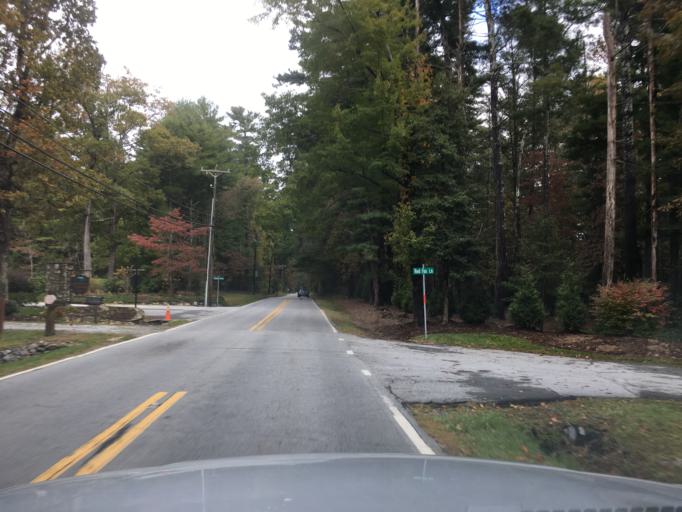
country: US
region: North Carolina
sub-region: Henderson County
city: Flat Rock
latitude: 35.2601
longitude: -82.4384
